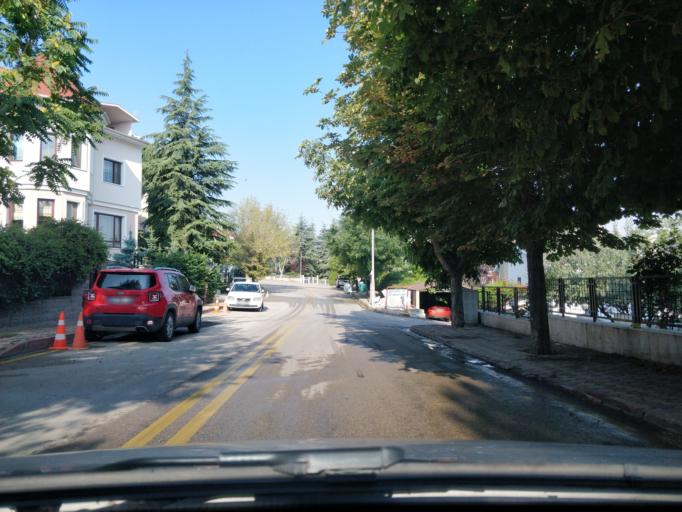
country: TR
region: Ankara
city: Batikent
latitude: 39.8950
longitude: 32.7213
